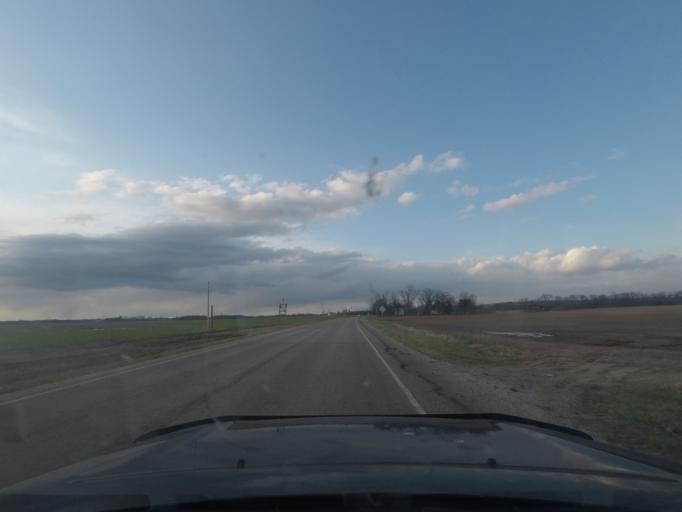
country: US
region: Indiana
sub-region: LaPorte County
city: Kingsford Heights
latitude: 41.5208
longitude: -86.7404
